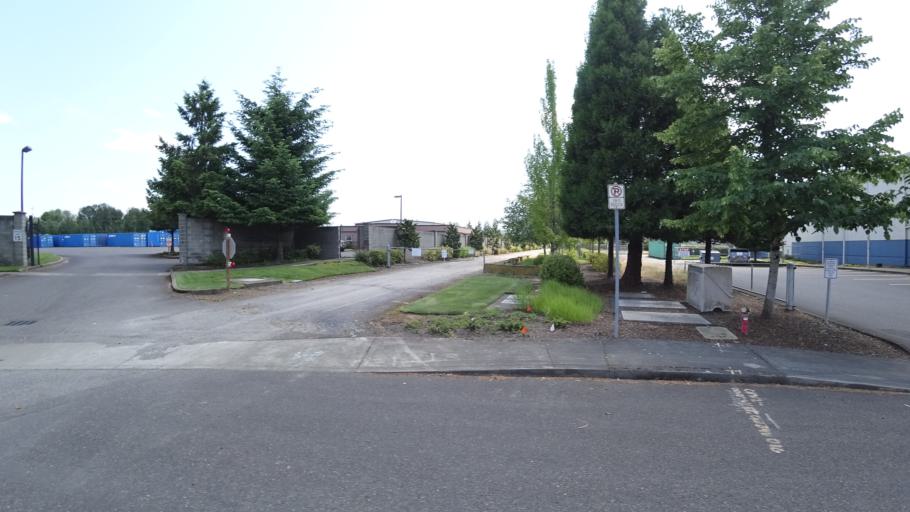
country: US
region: Oregon
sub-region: Washington County
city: West Haven
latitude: 45.6184
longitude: -122.7675
